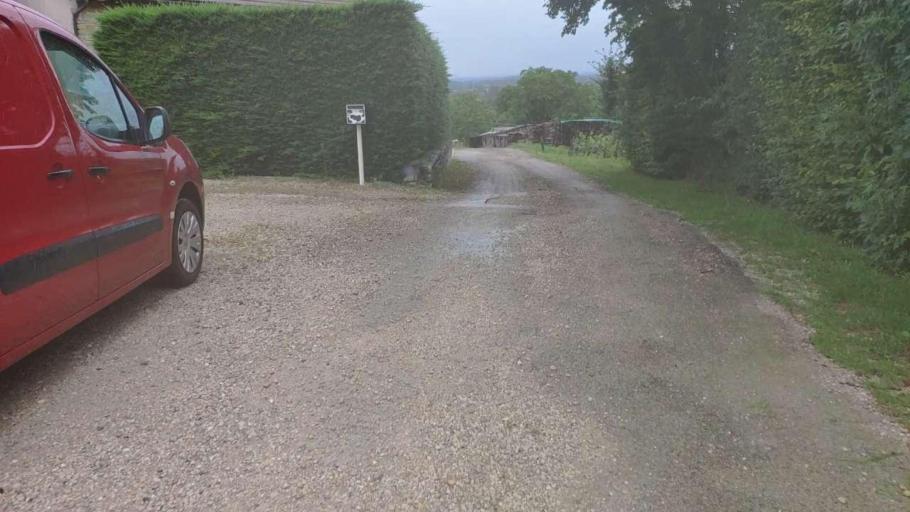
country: FR
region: Franche-Comte
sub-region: Departement du Jura
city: Poligny
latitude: 46.7911
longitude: 5.6144
